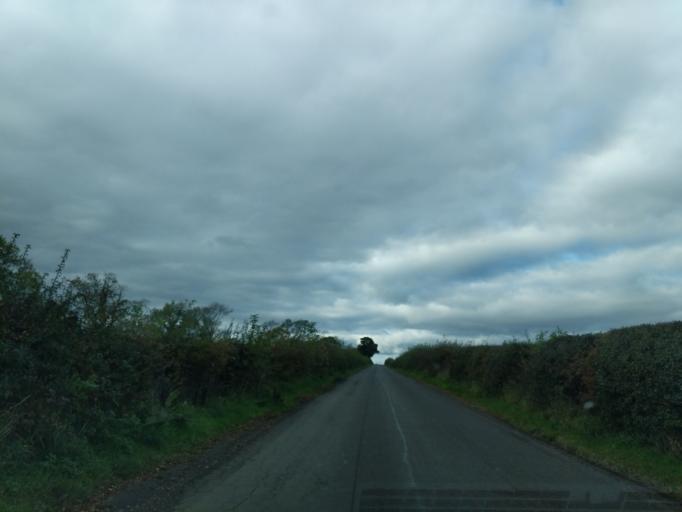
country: GB
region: Scotland
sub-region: East Lothian
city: Haddington
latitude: 55.9293
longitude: -2.8278
